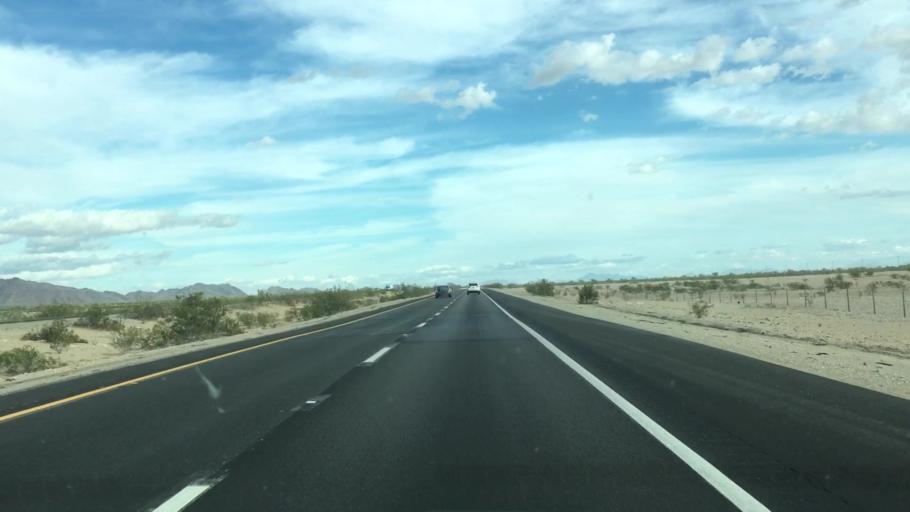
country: US
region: California
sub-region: Riverside County
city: Mesa Verde
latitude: 33.6088
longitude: -114.8656
